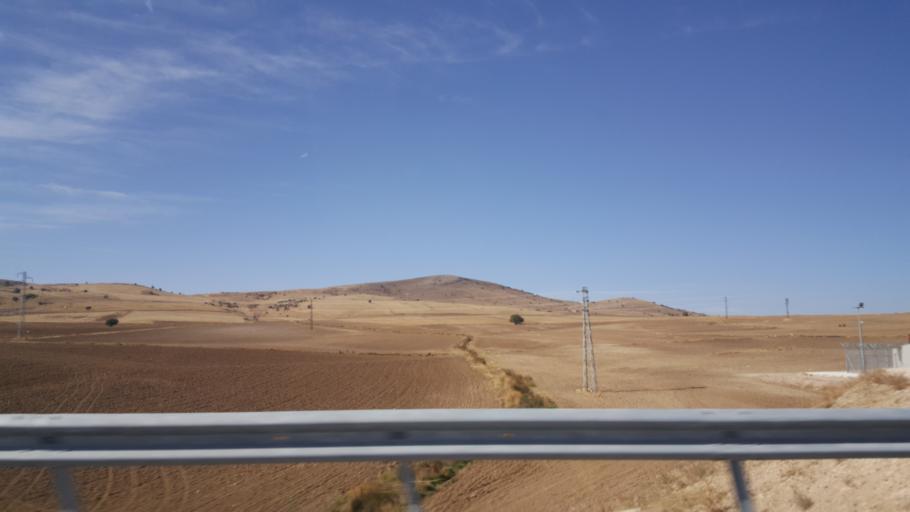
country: TR
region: Ankara
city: Ikizce
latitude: 39.5542
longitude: 32.6552
